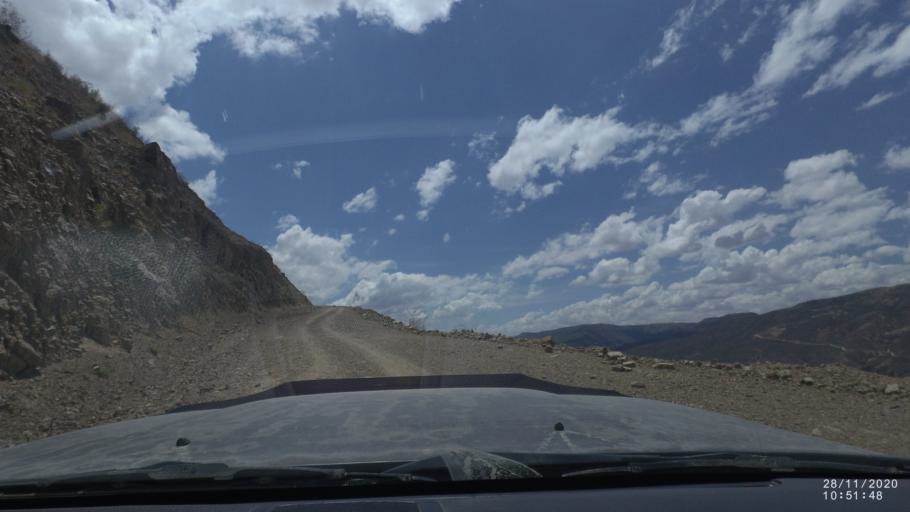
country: BO
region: Cochabamba
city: Capinota
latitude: -17.7849
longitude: -66.1228
